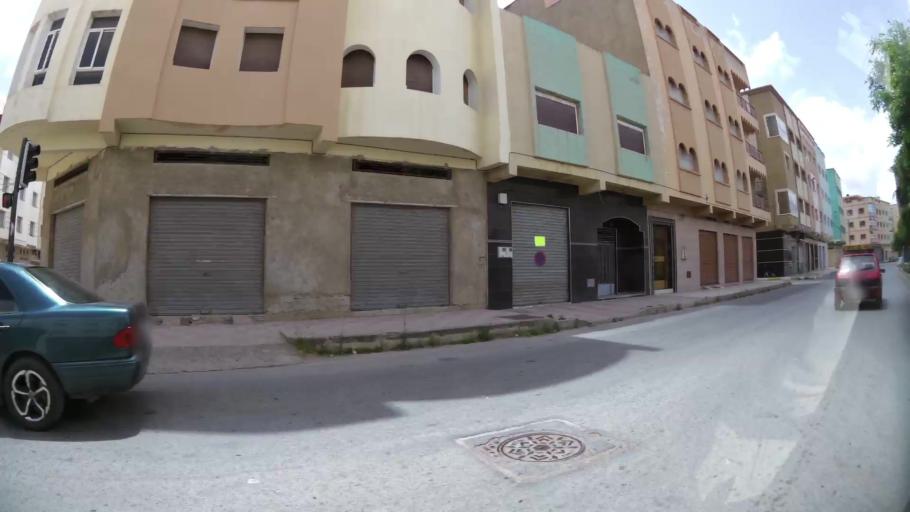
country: MA
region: Oriental
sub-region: Nador
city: Nador
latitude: 35.1689
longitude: -2.9196
